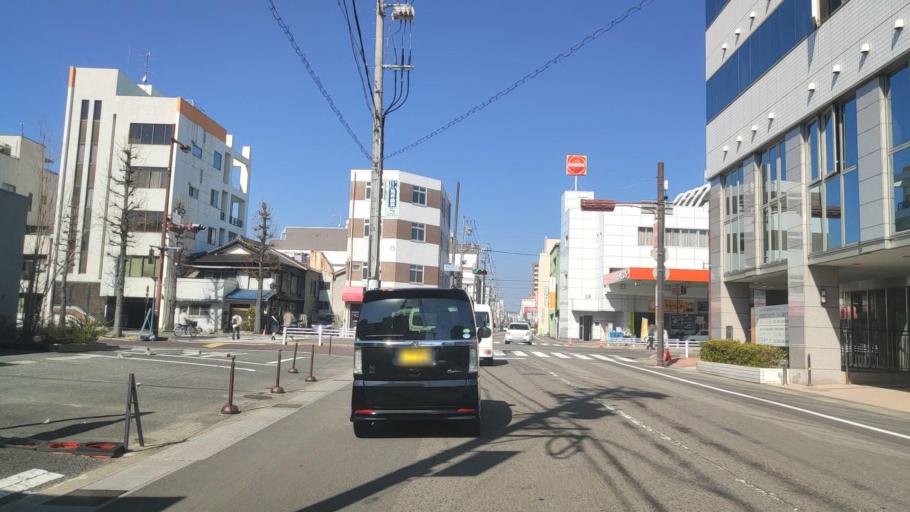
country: JP
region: Gifu
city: Gifu-shi
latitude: 35.4145
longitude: 136.7620
